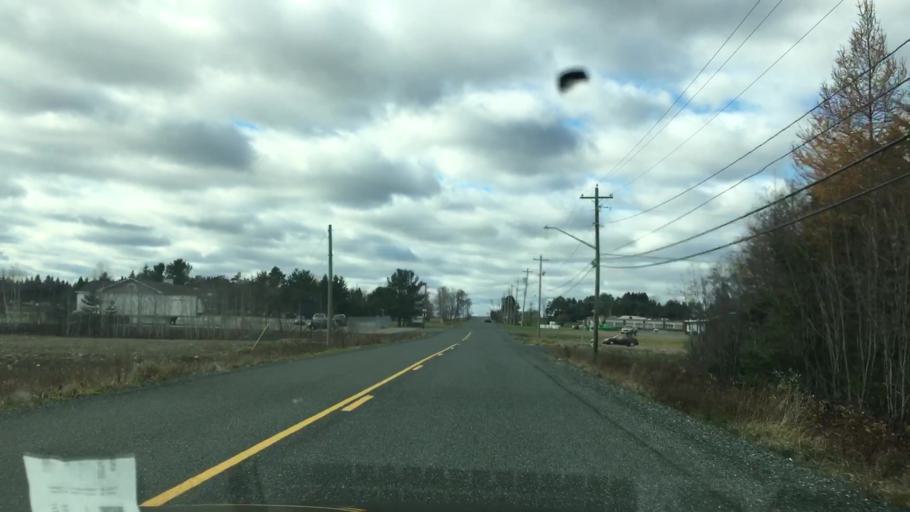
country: CA
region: New Brunswick
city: Florenceville-Bristol
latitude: 46.2888
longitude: -67.5415
